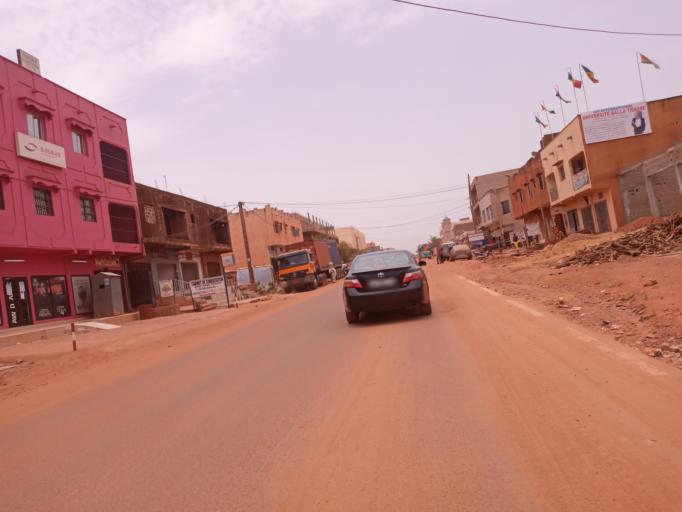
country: ML
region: Bamako
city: Bamako
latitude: 12.5802
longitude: -8.0177
